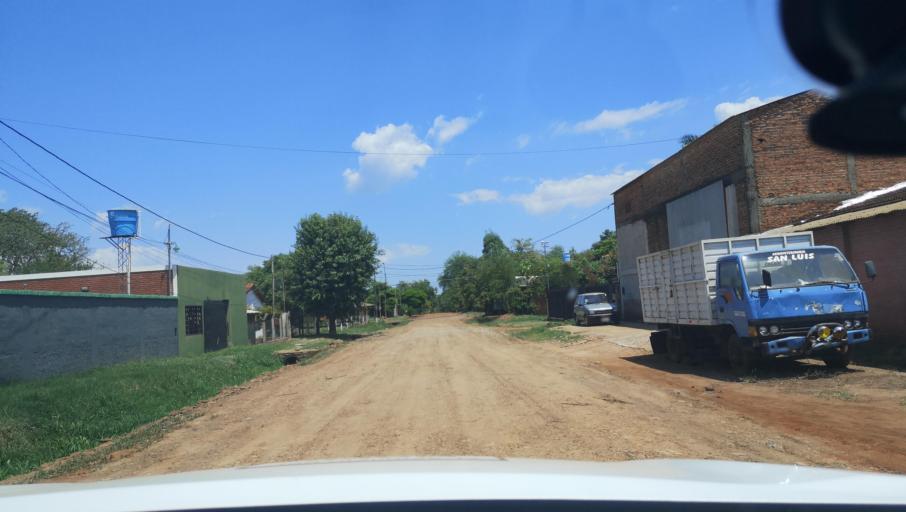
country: PY
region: Itapua
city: Carmen del Parana
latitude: -27.1653
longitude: -56.2351
